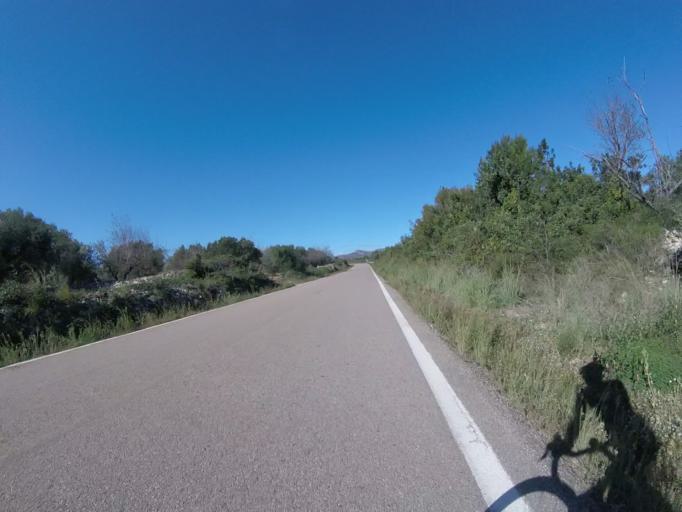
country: ES
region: Valencia
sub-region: Provincia de Castello
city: Chert/Xert
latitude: 40.4567
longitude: 0.1464
